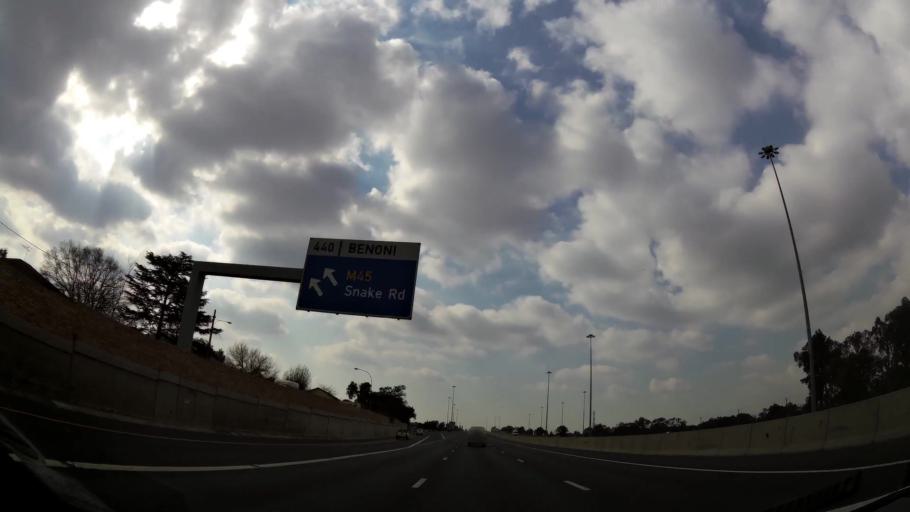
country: ZA
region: Gauteng
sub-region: Ekurhuleni Metropolitan Municipality
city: Benoni
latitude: -26.1767
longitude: 28.3295
